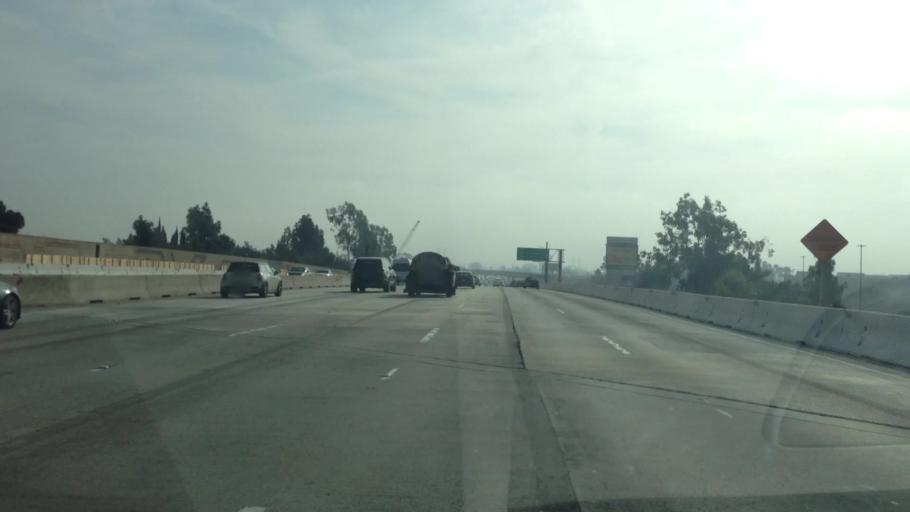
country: US
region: California
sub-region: Orange County
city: Westminster
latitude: 33.7509
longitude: -118.0124
